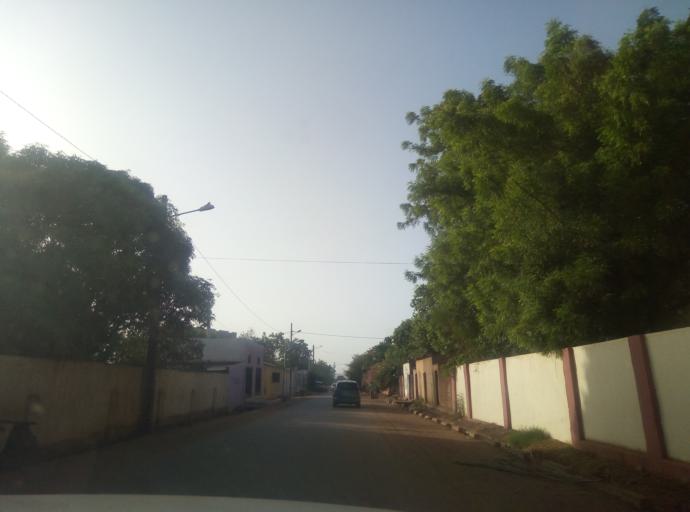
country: ML
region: Bamako
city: Bamako
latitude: 12.6069
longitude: -7.9716
